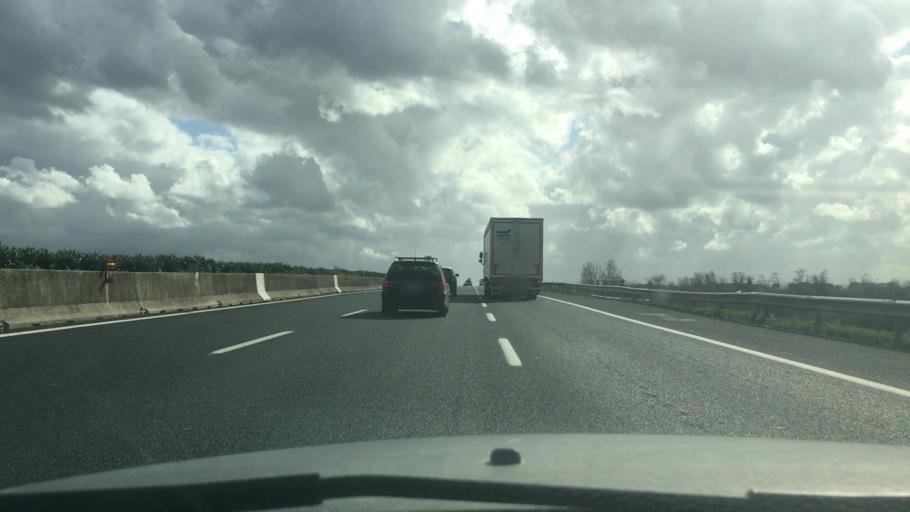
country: IT
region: Campania
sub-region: Provincia di Napoli
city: Pascarola
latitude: 41.0030
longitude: 14.3236
